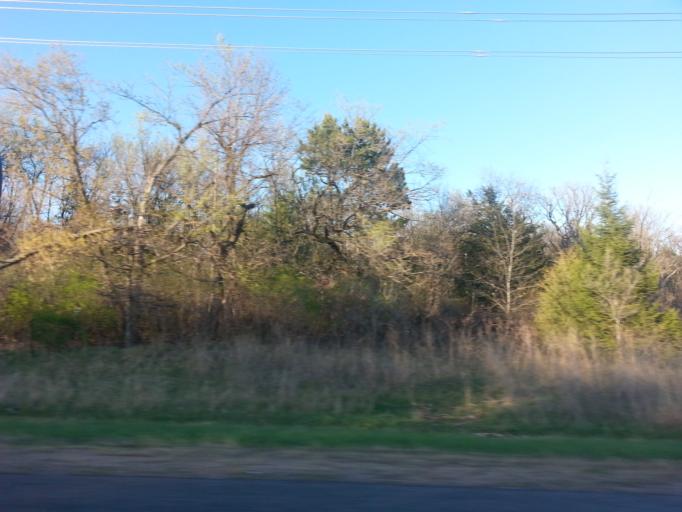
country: US
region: Wisconsin
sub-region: Pierce County
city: Prescott
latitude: 44.6656
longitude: -92.7801
